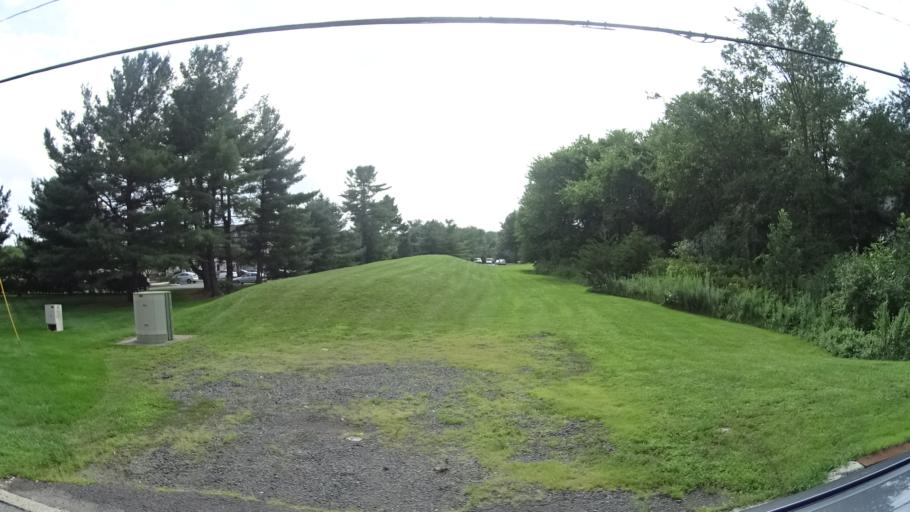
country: US
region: New Jersey
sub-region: Somerset County
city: Warren Township
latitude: 40.6558
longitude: -74.5294
